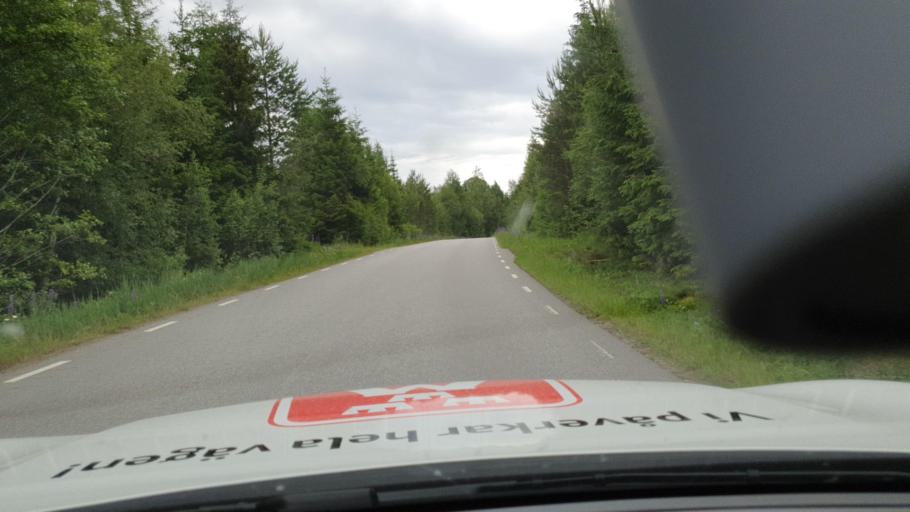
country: SE
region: Vaestra Goetaland
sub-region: Karlsborgs Kommun
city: Karlsborg
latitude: 58.6690
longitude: 14.4312
